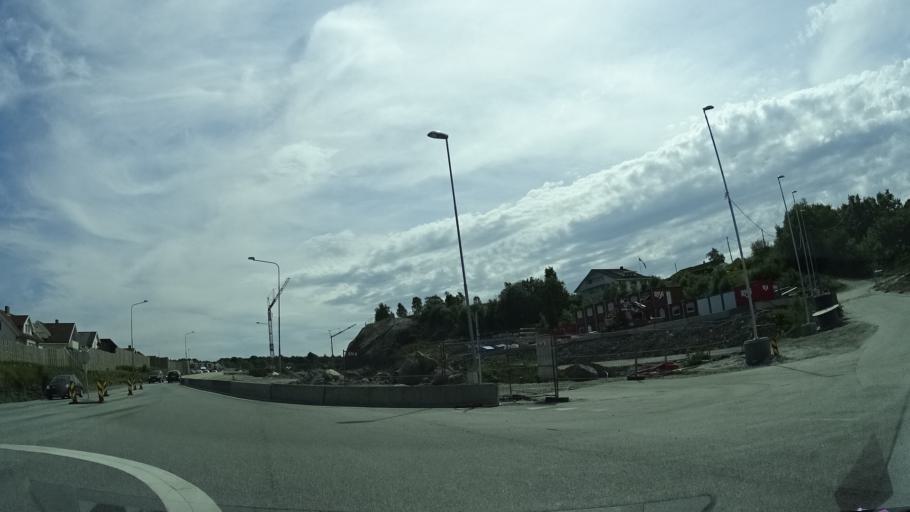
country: NO
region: Rogaland
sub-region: Stavanger
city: Stavanger
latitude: 58.9802
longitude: 5.6835
